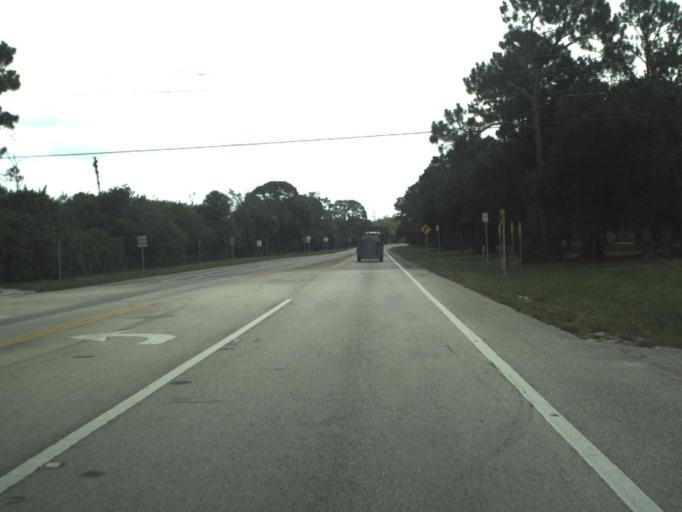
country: US
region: Florida
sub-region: Martin County
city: Palm City
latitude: 27.0952
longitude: -80.2741
